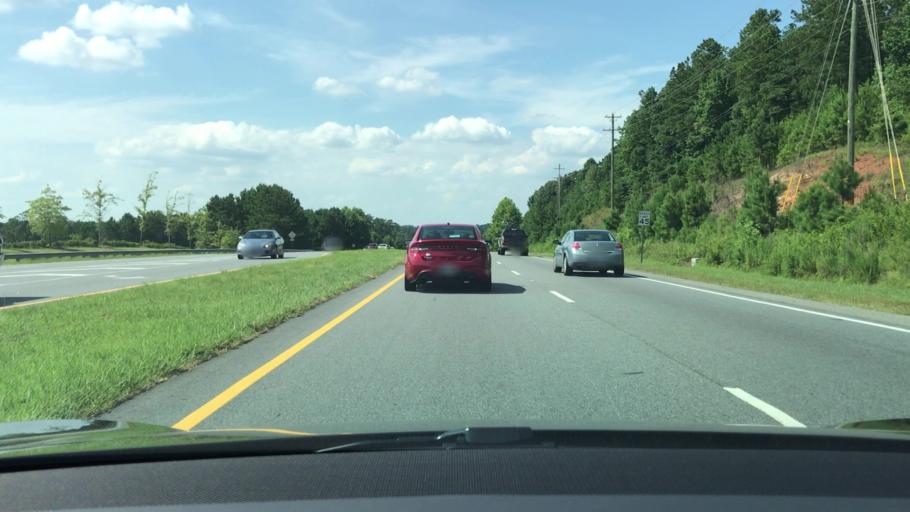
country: US
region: Georgia
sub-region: Fulton County
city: Johns Creek
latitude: 34.1021
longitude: -84.2163
